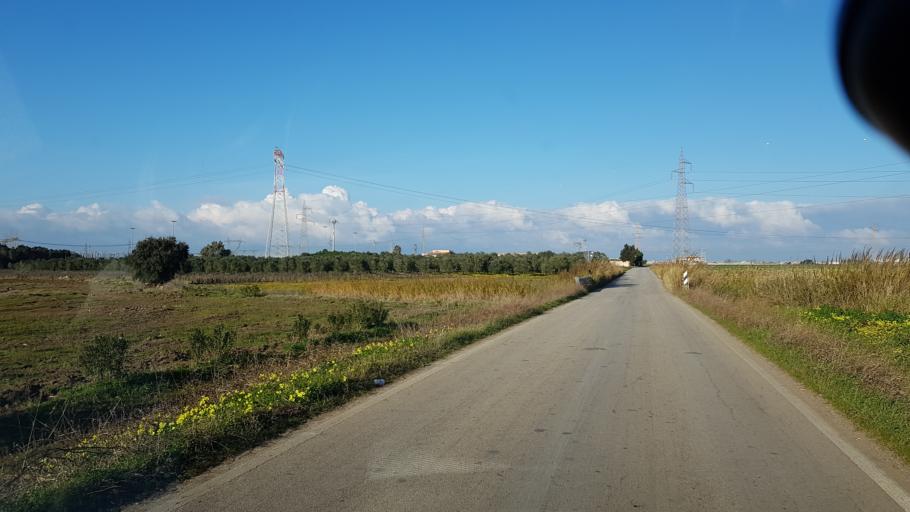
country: IT
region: Apulia
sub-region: Provincia di Brindisi
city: Brindisi
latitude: 40.5955
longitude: 17.9045
